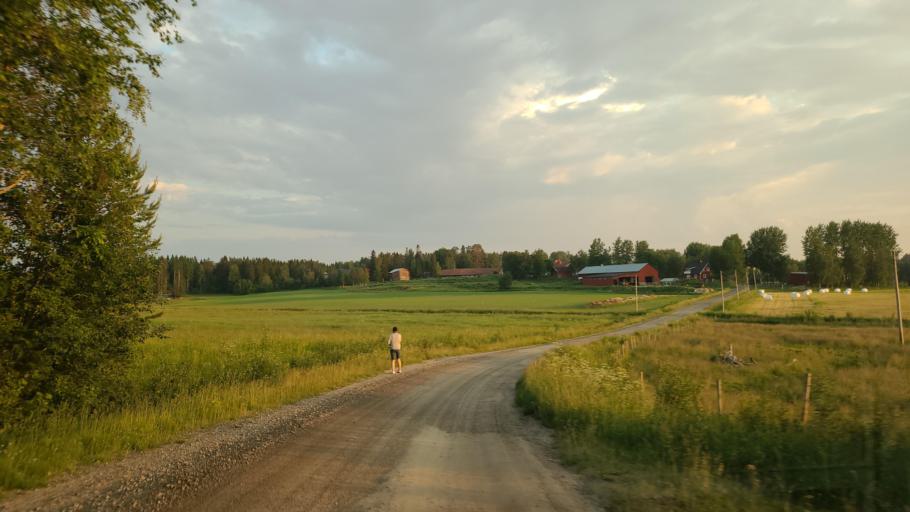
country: SE
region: Vaesterbotten
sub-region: Robertsfors Kommun
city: Robertsfors
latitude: 64.0661
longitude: 20.8712
